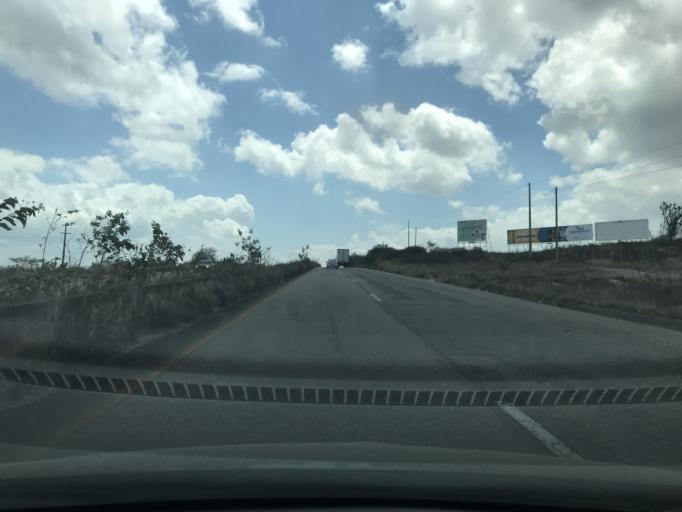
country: BR
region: Pernambuco
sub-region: Caruaru
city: Caruaru
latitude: -8.3042
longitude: -35.9286
